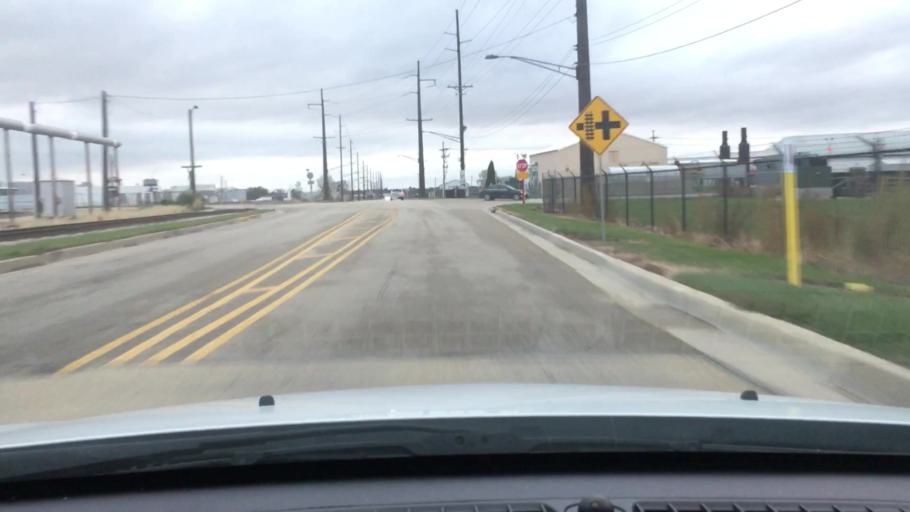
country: US
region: Illinois
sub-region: Ogle County
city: Rochelle
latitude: 41.9072
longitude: -89.0464
